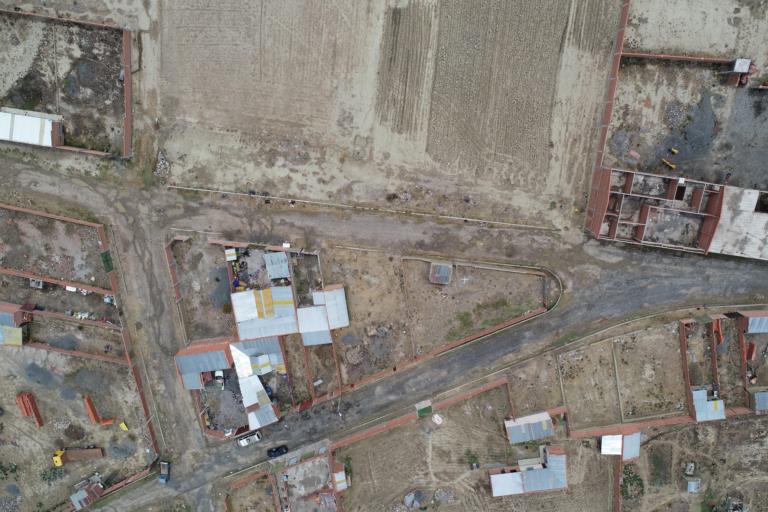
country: BO
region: La Paz
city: Achacachi
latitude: -16.0532
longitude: -68.6830
